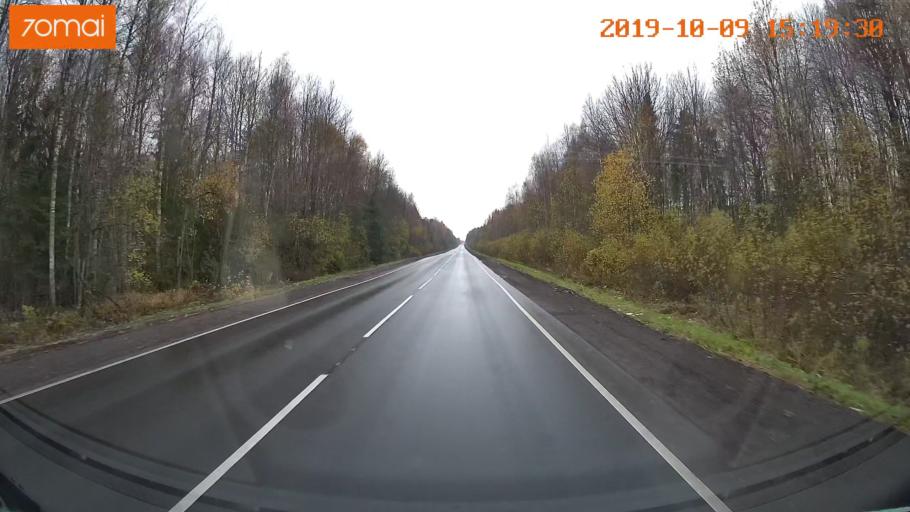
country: RU
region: Kostroma
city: Susanino
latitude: 58.0750
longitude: 41.5553
